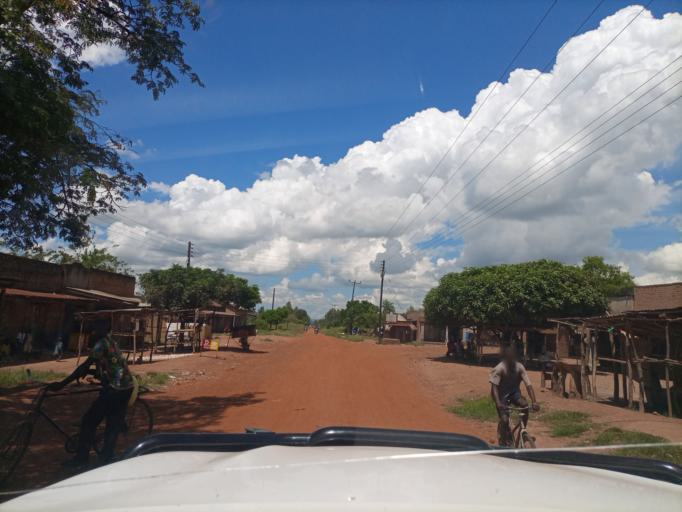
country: UG
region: Eastern Region
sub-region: Tororo District
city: Tororo
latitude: 0.6695
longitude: 34.0034
